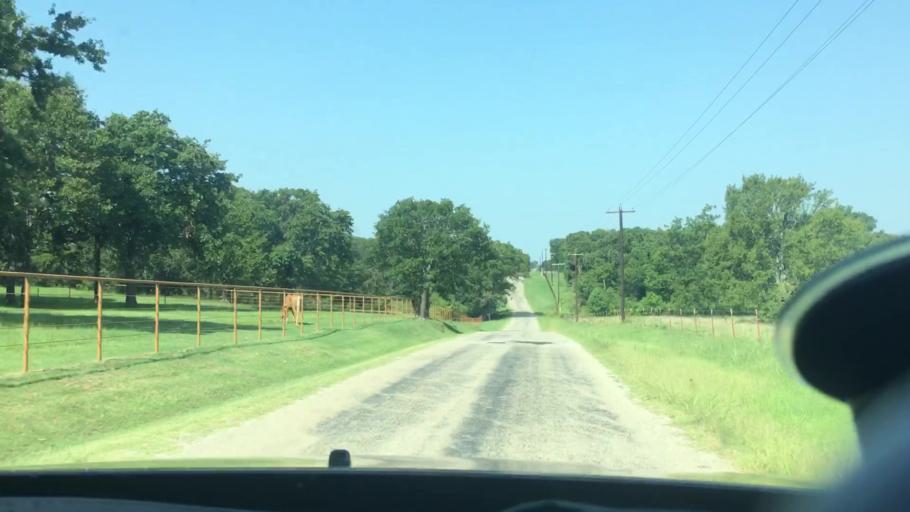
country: US
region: Oklahoma
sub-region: Bryan County
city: Durant
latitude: 34.0121
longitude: -96.4452
